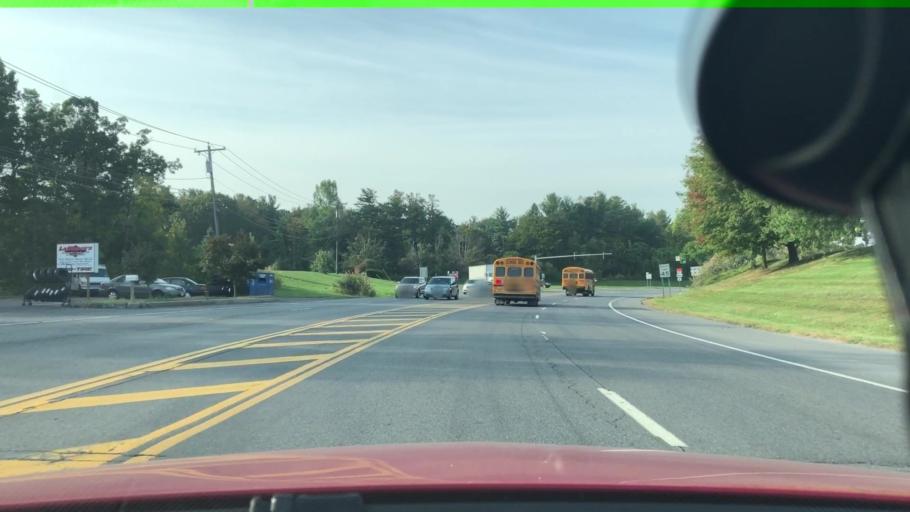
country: US
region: New York
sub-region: Albany County
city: Albany
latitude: 42.6222
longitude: -73.7775
